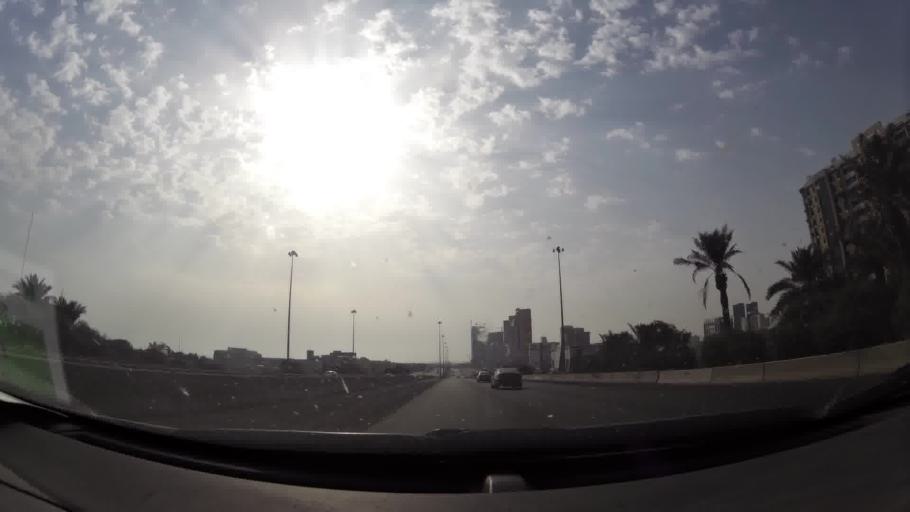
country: KW
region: Mubarak al Kabir
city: Sabah as Salim
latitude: 29.2669
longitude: 48.0849
